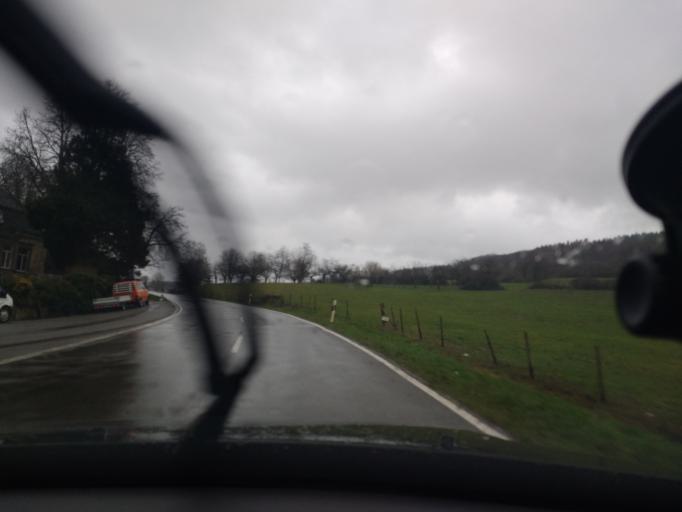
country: DE
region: Rheinland-Pfalz
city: Wiltingen
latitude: 49.6502
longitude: 6.6120
